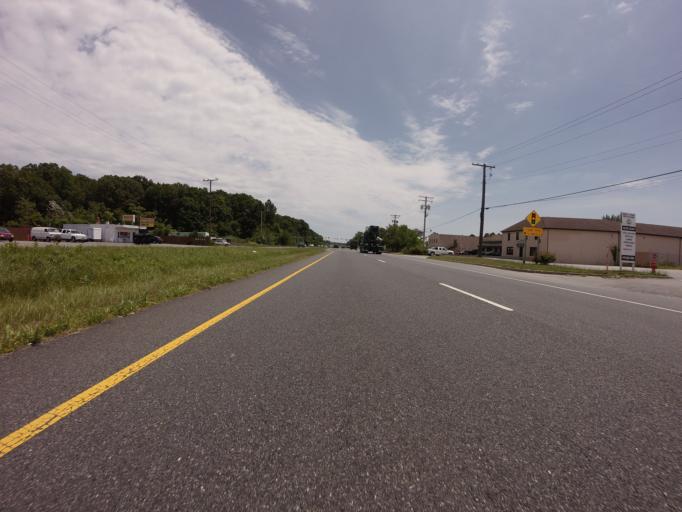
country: US
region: Maryland
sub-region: Baltimore County
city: Essex
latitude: 39.2813
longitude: -76.4869
